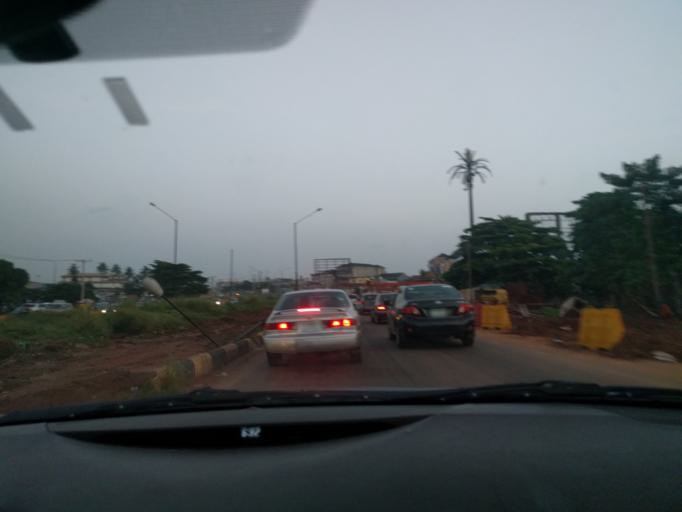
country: NG
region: Lagos
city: Oshodi
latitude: 6.5559
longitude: 3.3228
